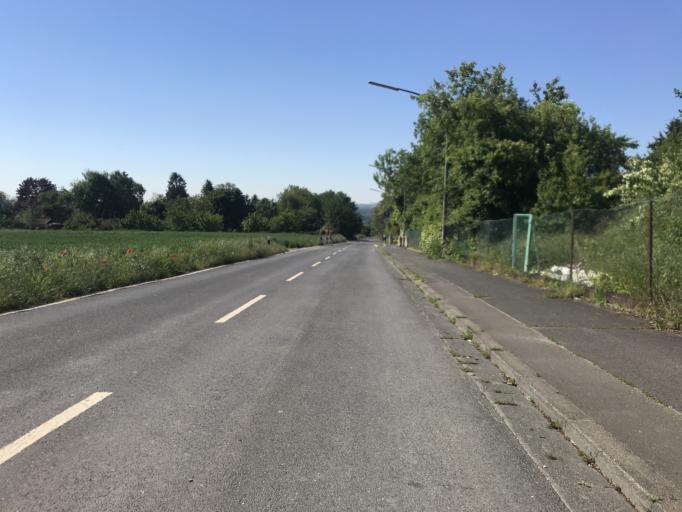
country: DE
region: Hesse
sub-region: Regierungsbezirk Darmstadt
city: Walluf
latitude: 50.0622
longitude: 8.1992
